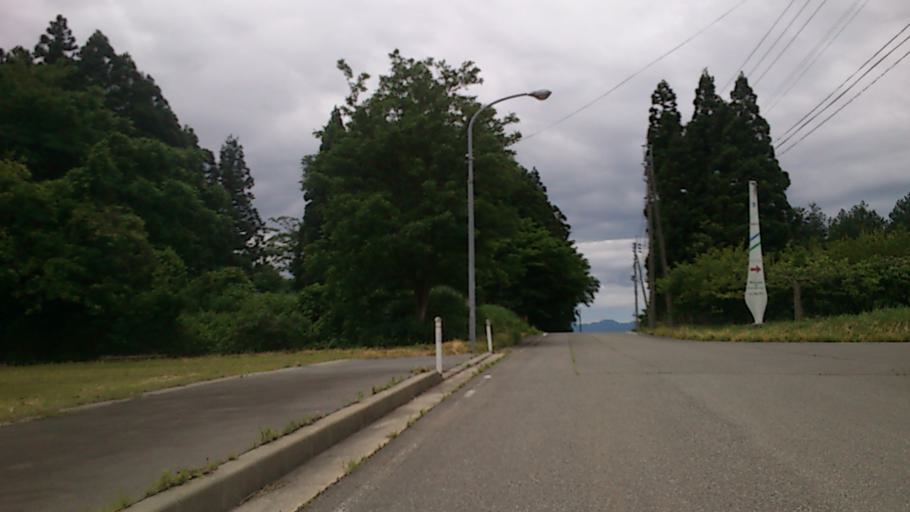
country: JP
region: Yamagata
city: Tsuruoka
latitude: 38.7834
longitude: 139.9755
